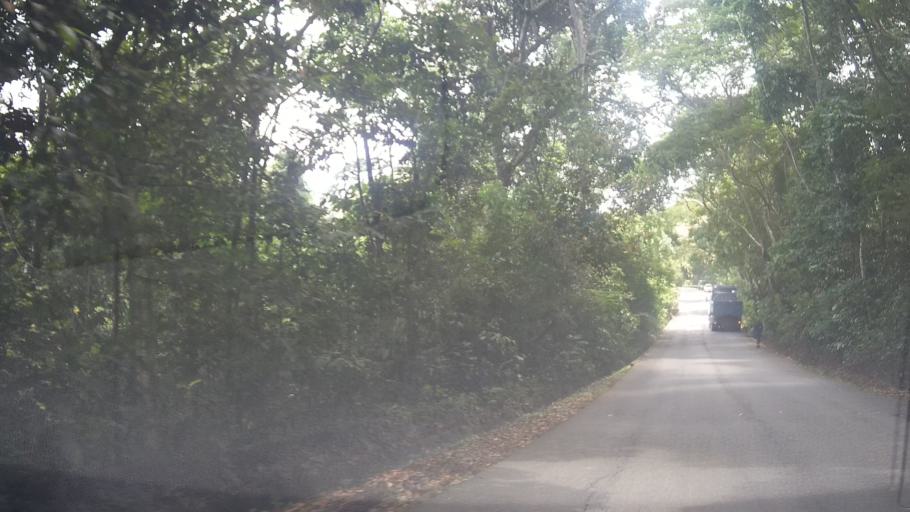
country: SG
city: Singapore
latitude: 1.3544
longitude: 103.7954
